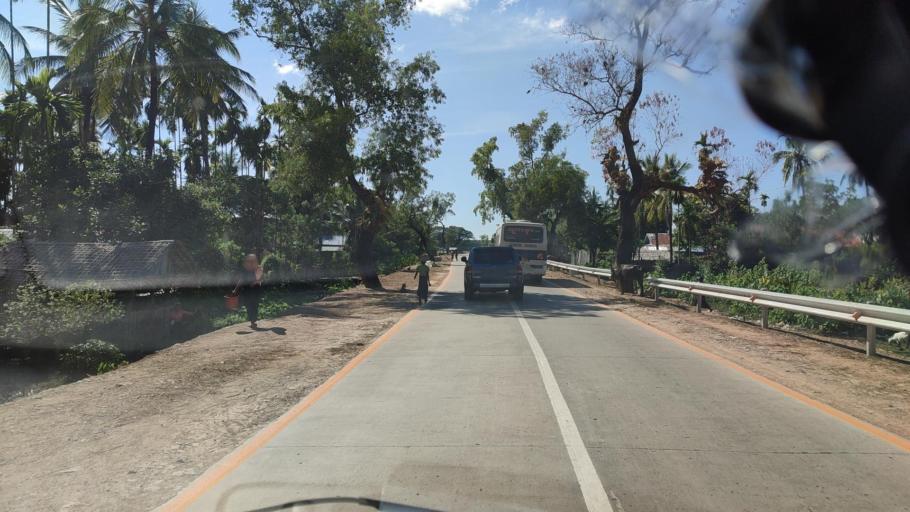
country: MM
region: Rakhine
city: Sittwe
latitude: 20.4784
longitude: 93.2871
